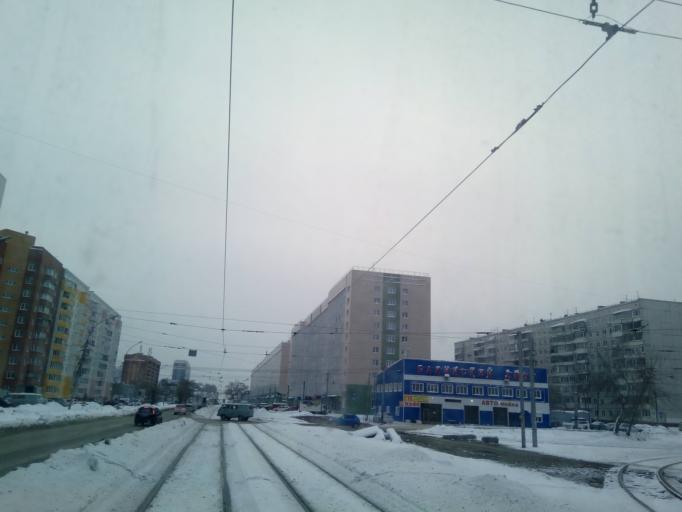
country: RU
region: Novosibirsk
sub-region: Novosibirskiy Rayon
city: Novosibirsk
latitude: 54.9926
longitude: 82.8567
